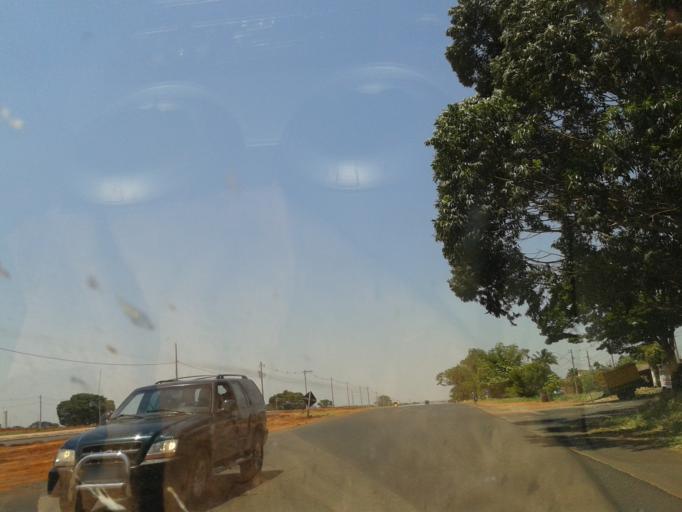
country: BR
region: Minas Gerais
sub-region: Uberlandia
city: Uberlandia
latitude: -18.9565
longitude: -48.3070
